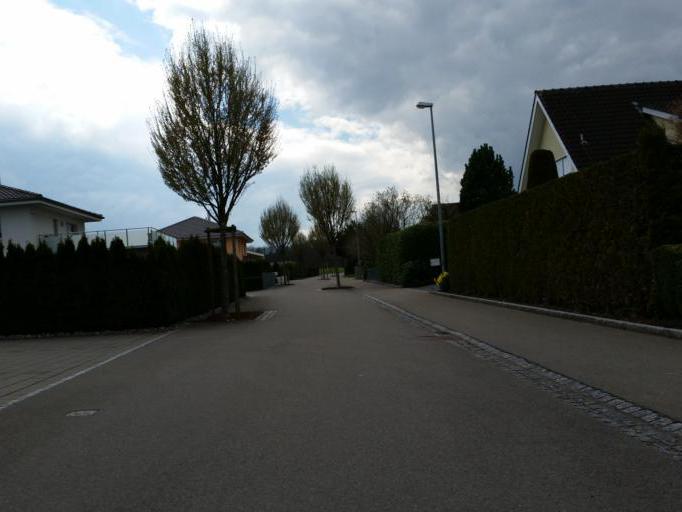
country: CH
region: Thurgau
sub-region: Arbon District
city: Uttwil
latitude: 47.5797
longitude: 9.3467
